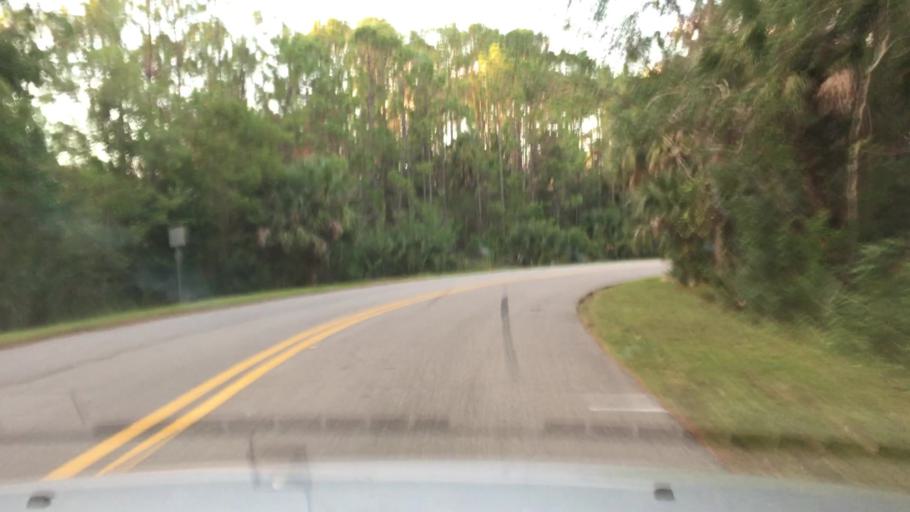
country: US
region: Florida
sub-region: Volusia County
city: Ormond Beach
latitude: 29.2815
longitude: -81.1237
